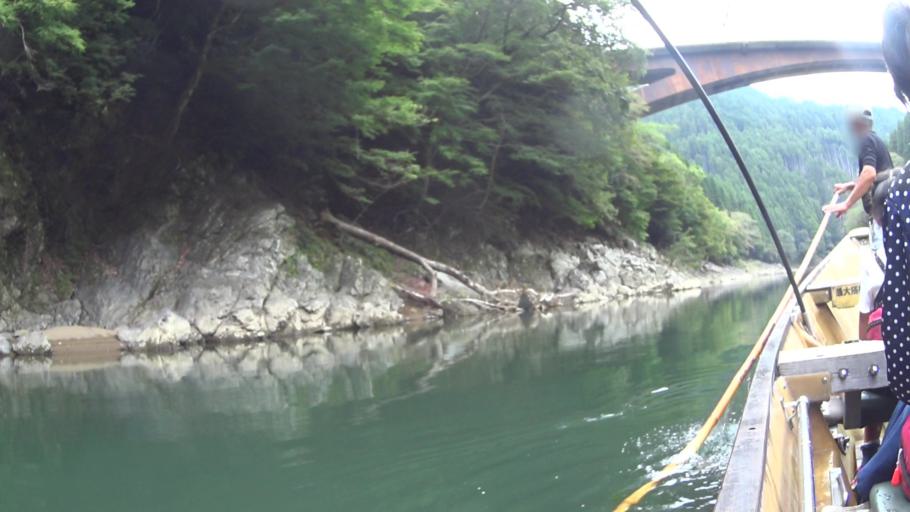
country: JP
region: Kyoto
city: Kameoka
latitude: 35.0218
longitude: 135.6263
